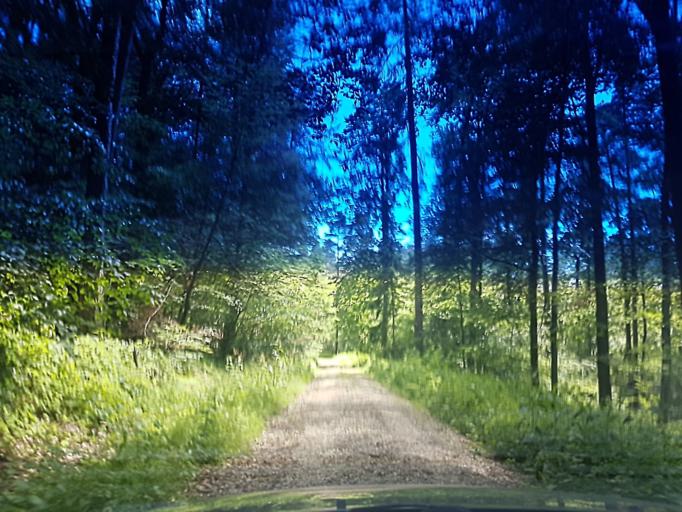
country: DE
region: Bavaria
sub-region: Upper Franconia
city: Litzendorf
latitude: 49.9408
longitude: 11.0239
